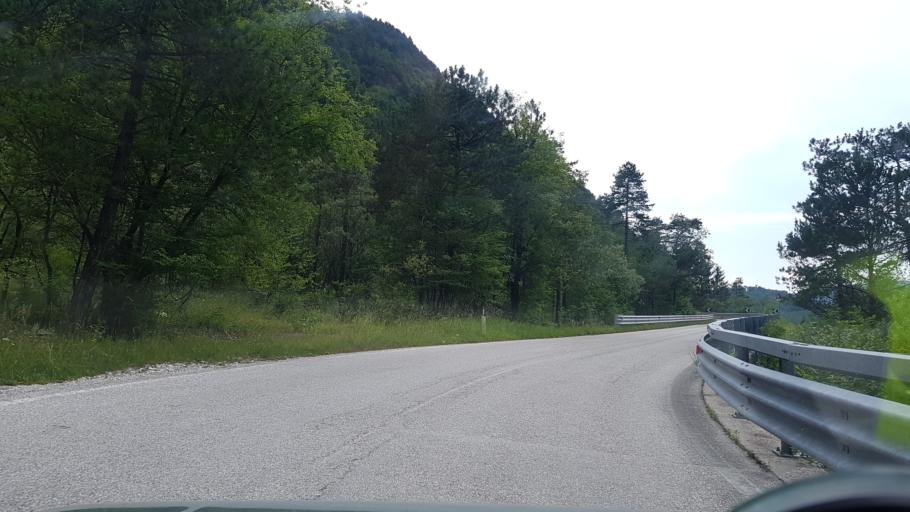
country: IT
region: Friuli Venezia Giulia
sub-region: Provincia di Udine
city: Lusevera
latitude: 46.2905
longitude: 13.2691
